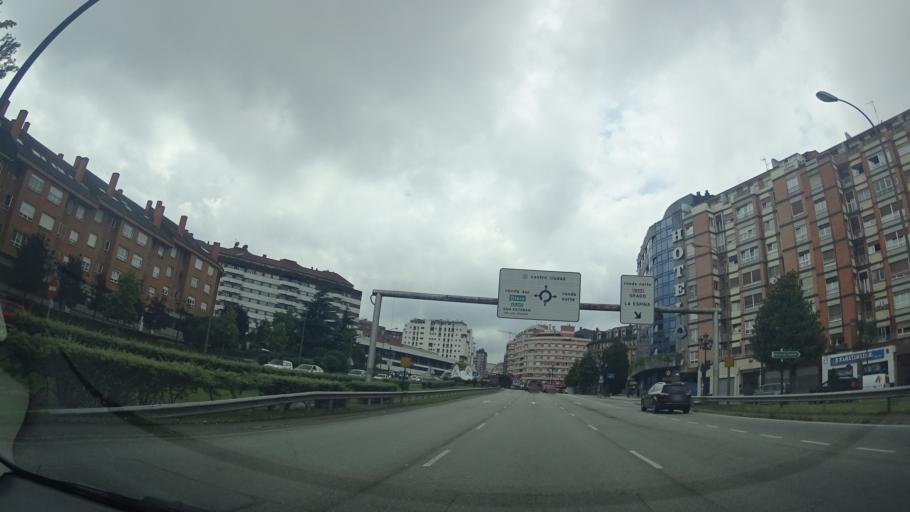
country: ES
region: Asturias
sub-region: Province of Asturias
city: Oviedo
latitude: 43.3667
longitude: -5.8403
